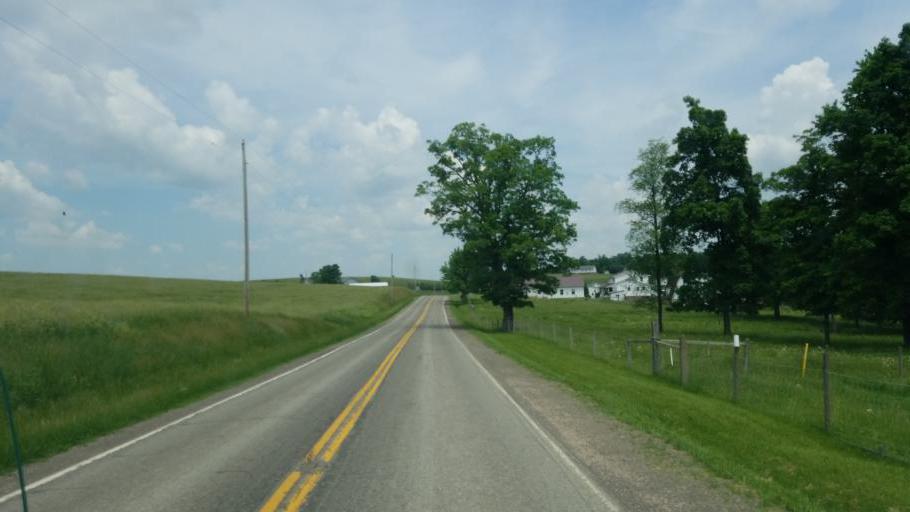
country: US
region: Ohio
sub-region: Coshocton County
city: West Lafayette
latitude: 40.4320
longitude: -81.7847
